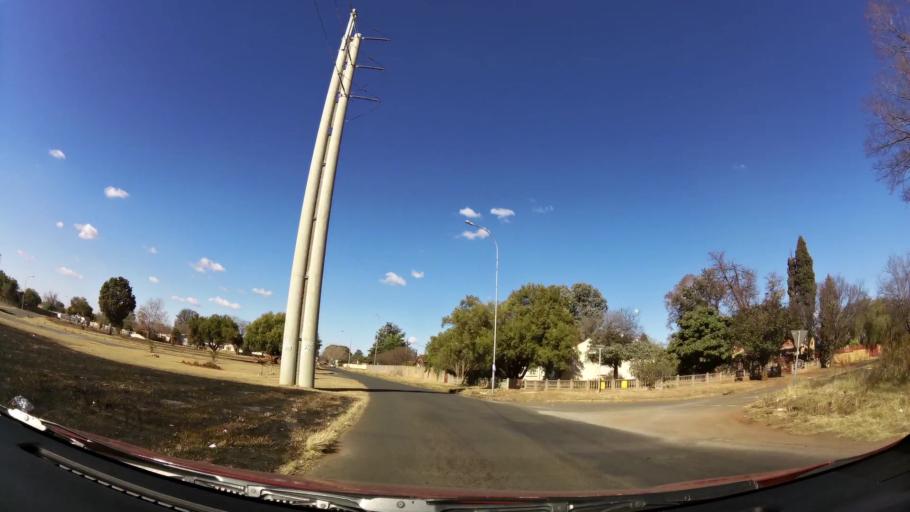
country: ZA
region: Gauteng
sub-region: West Rand District Municipality
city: Carletonville
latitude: -26.3693
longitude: 27.3840
